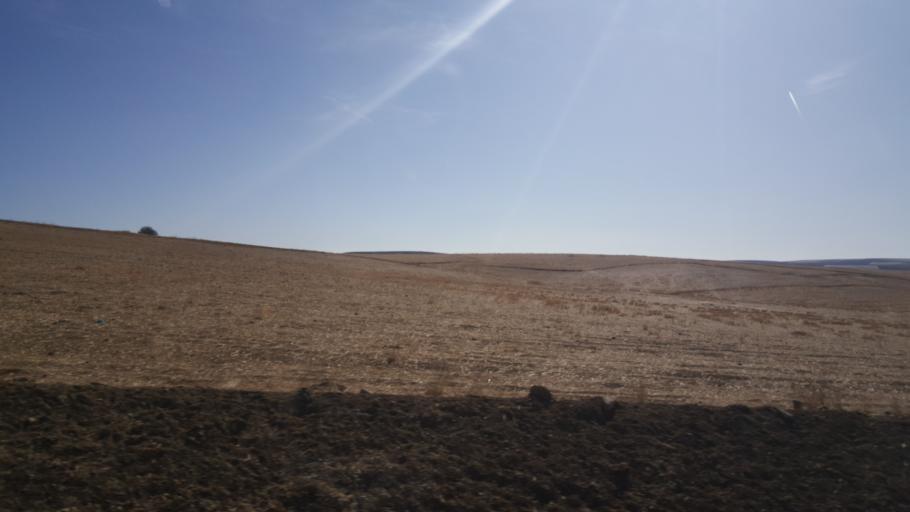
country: TR
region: Ankara
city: Yenice
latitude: 39.2913
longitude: 32.6318
